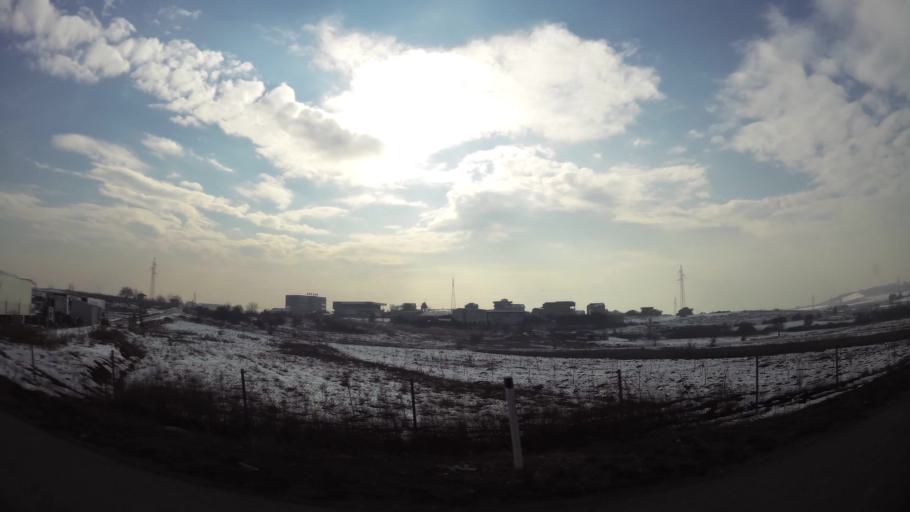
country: MK
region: Suto Orizari
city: Suto Orizare
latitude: 42.0513
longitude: 21.4279
